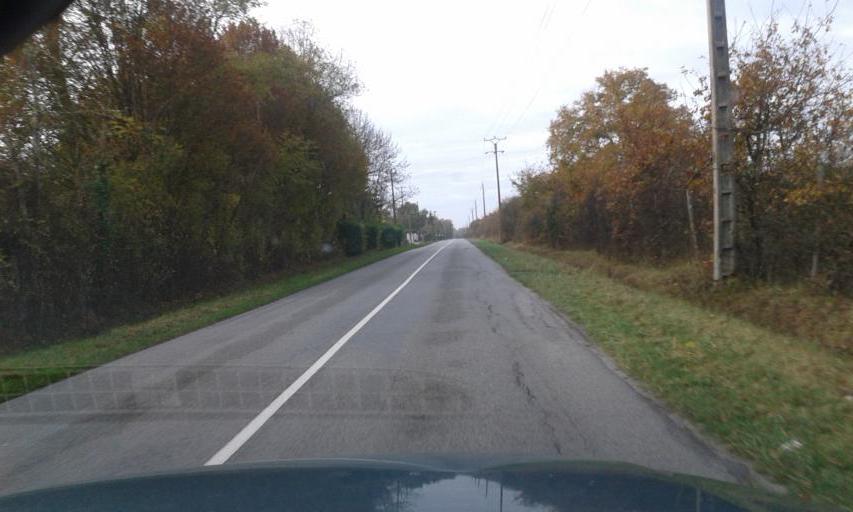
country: FR
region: Centre
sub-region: Departement du Loiret
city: Jouy-le-Potier
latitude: 47.7758
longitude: 1.8684
